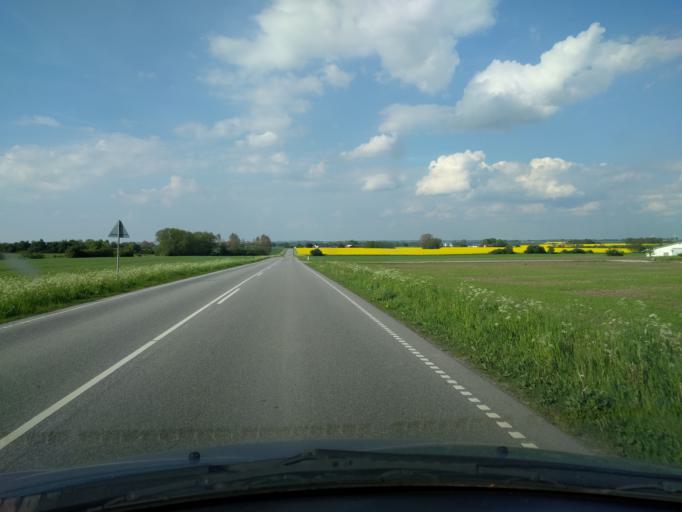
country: DK
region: Zealand
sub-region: Slagelse Kommune
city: Skaelskor
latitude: 55.3014
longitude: 11.2871
